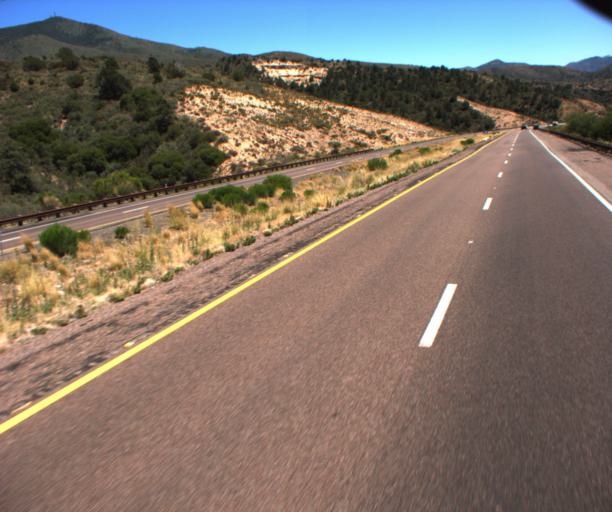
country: US
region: Arizona
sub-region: Gila County
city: Tonto Basin
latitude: 33.9173
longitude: -111.4541
